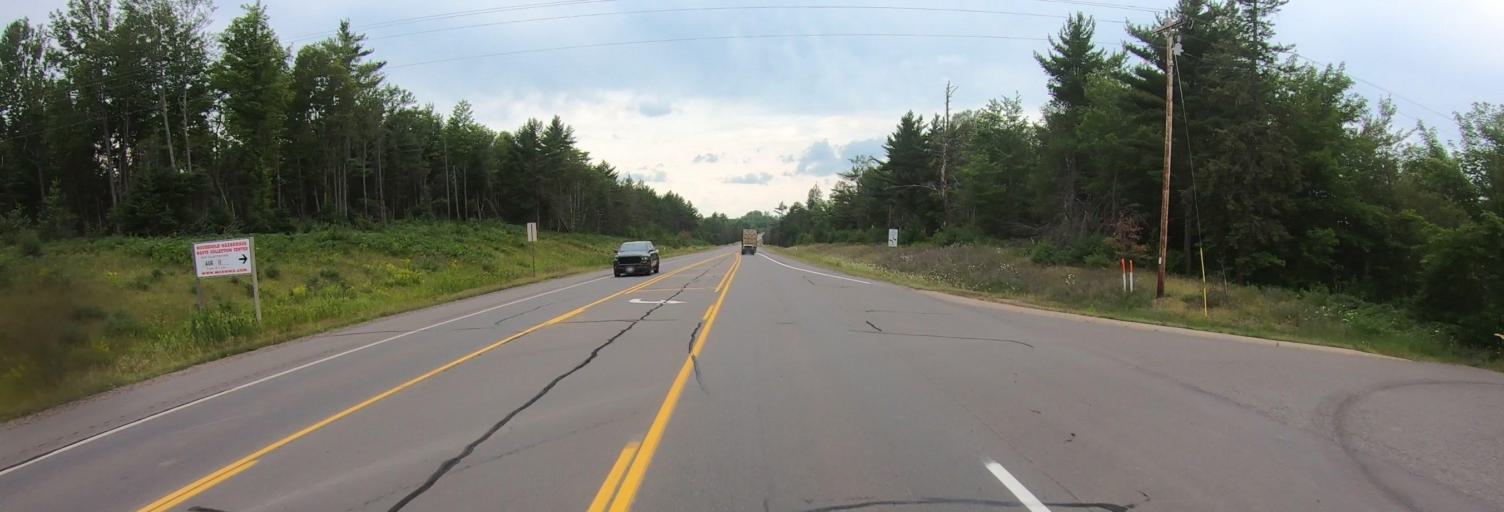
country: US
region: Michigan
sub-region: Marquette County
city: West Ishpeming
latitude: 46.4860
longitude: -87.7385
